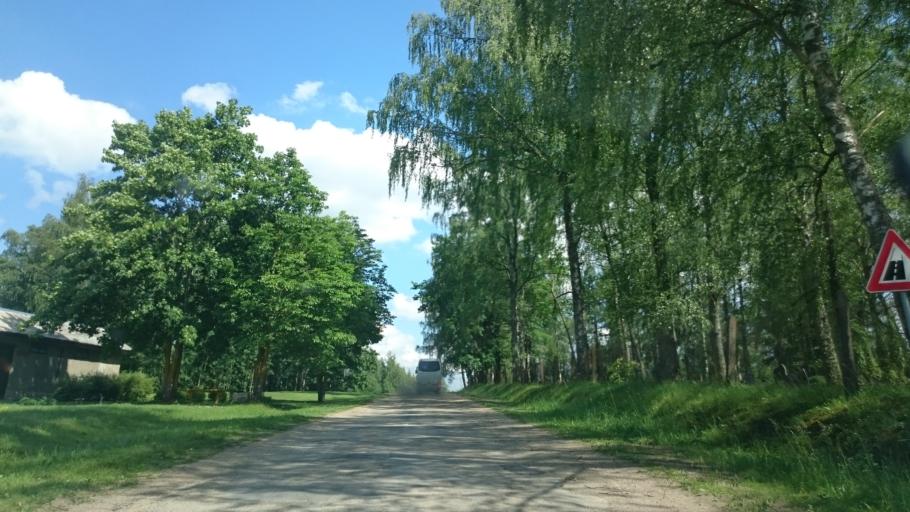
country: LV
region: Cibla
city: Cibla
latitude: 56.5653
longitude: 27.8037
